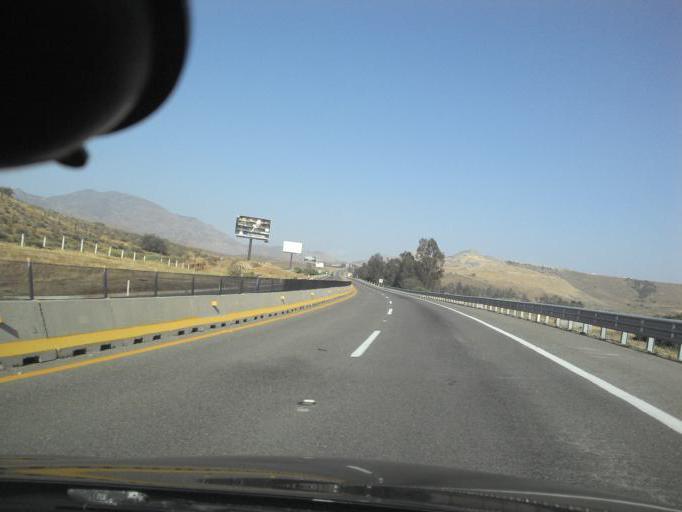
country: MX
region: Baja California
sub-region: Tijuana
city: El Nino
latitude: 32.5459
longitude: -116.7919
